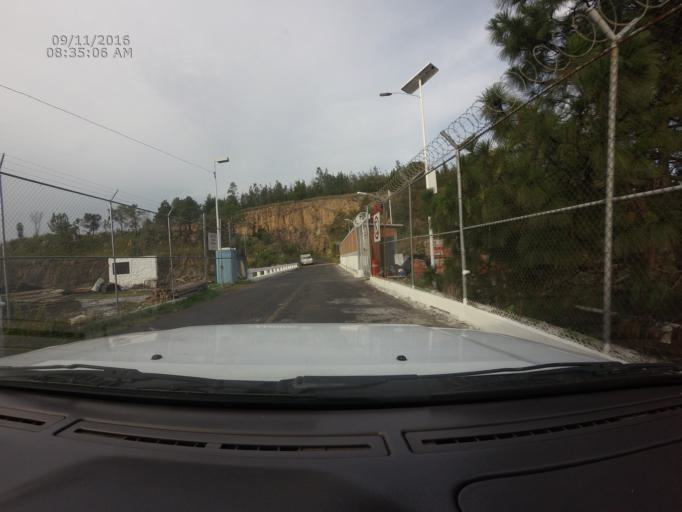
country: MX
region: Michoacan
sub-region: Morelia
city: La Mintzita (Piedra Dura)
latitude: 19.6291
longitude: -101.2601
